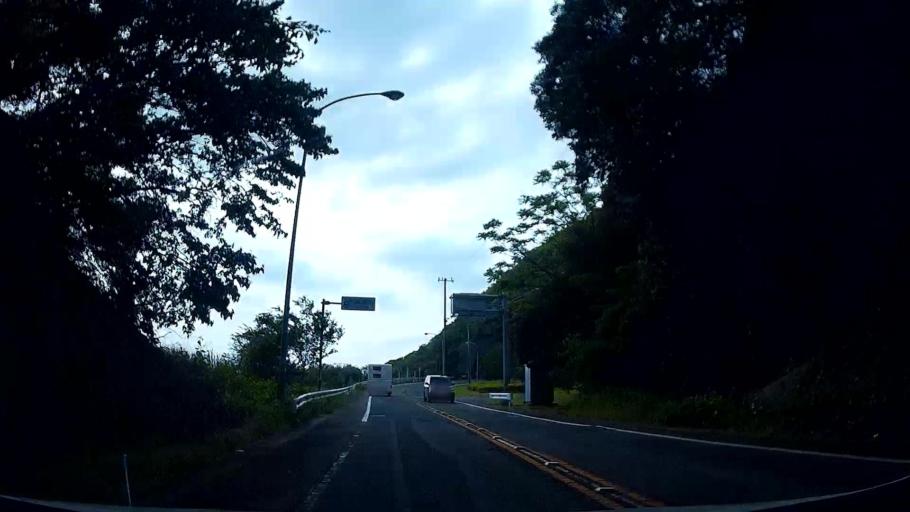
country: JP
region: Shizuoka
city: Heda
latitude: 34.8614
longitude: 138.7697
